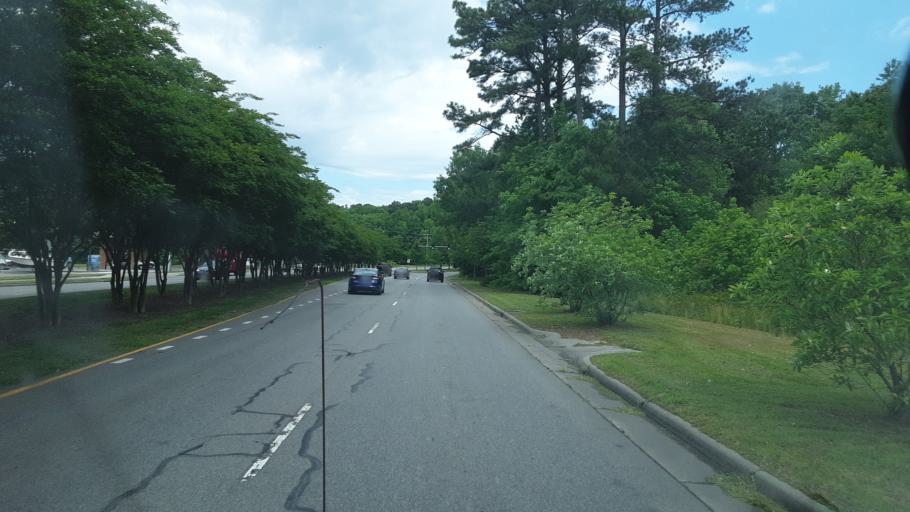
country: US
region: Virginia
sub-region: City of Virginia Beach
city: Virginia Beach
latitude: 36.7992
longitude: -76.0030
